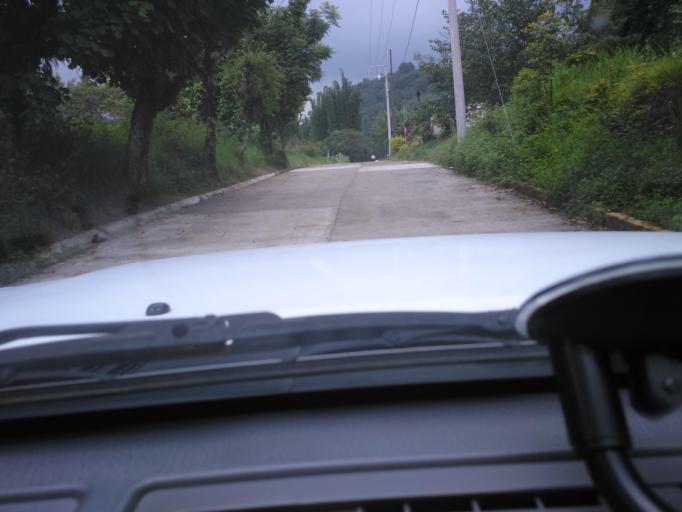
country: MX
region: Veracruz
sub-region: Mariano Escobedo
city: Chicola
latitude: 18.9112
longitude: -97.1096
